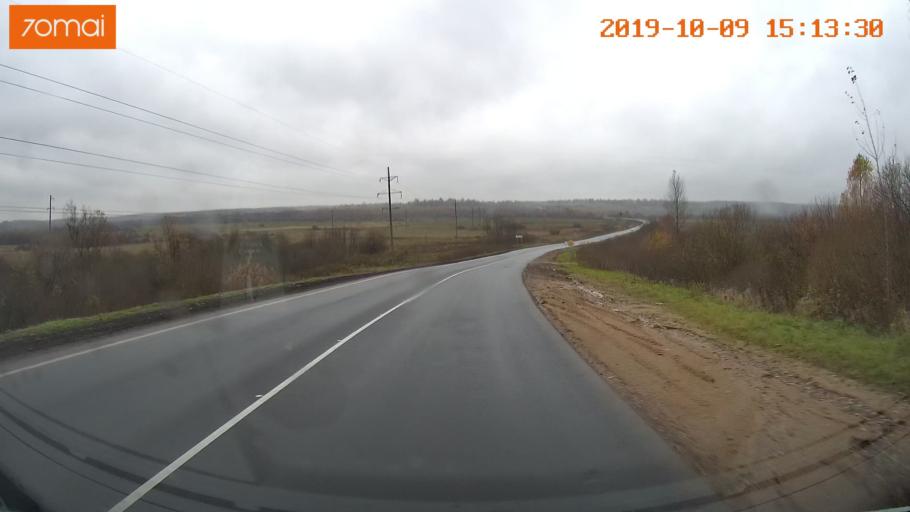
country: RU
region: Kostroma
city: Susanino
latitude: 58.1454
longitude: 41.6152
